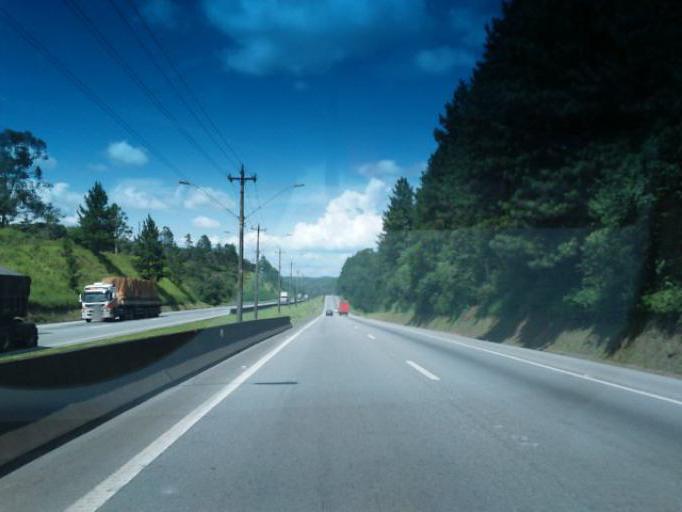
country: BR
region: Sao Paulo
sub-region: Sao Lourenco Da Serra
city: Sao Lourenco da Serra
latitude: -23.8686
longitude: -46.9558
